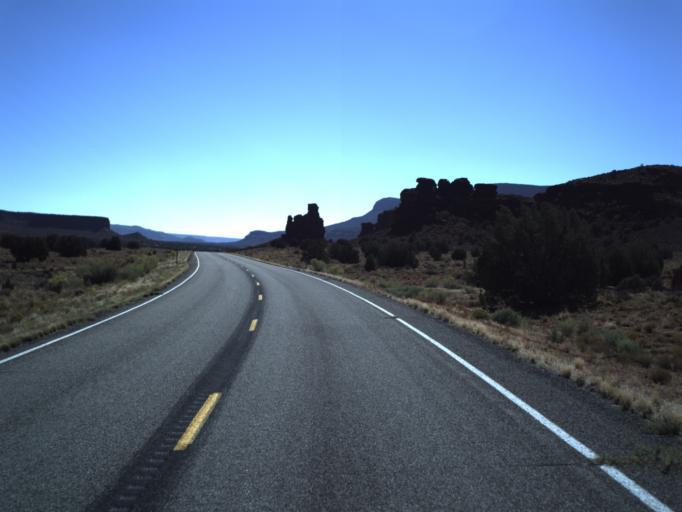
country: US
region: Utah
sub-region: San Juan County
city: Blanding
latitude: 37.7060
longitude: -110.2408
